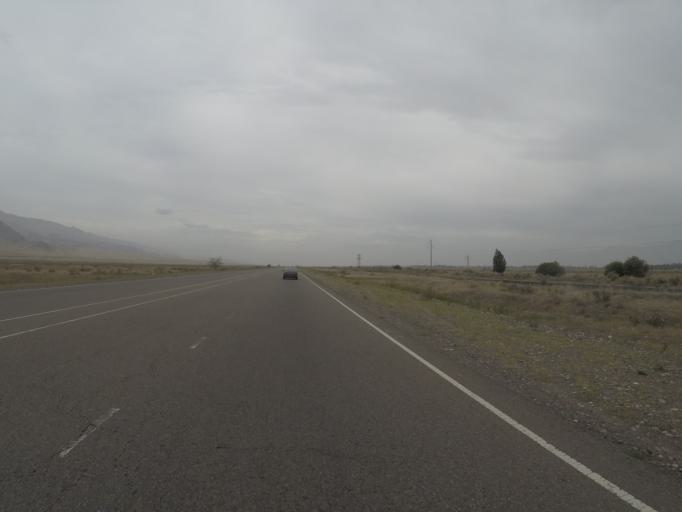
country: KG
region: Chuy
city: Tokmok
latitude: 42.8296
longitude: 75.4866
